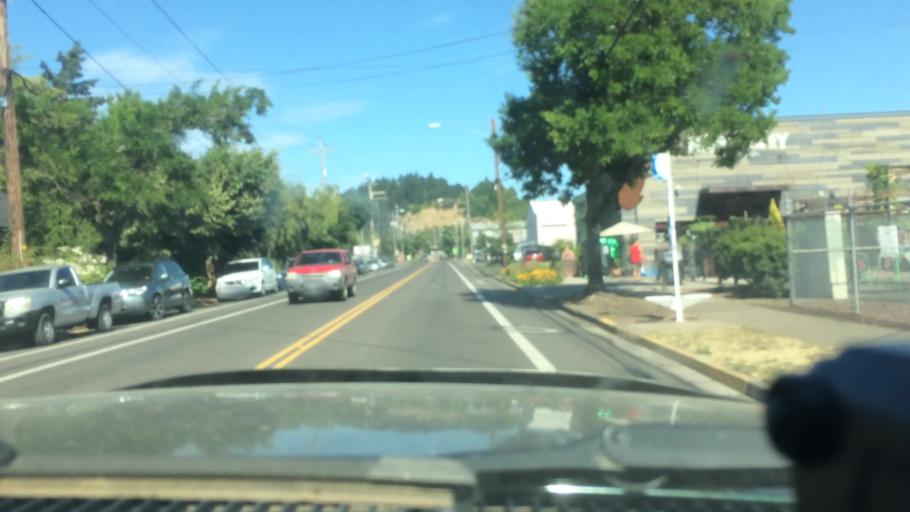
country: US
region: Oregon
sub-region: Lane County
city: Eugene
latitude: 44.0587
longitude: -123.1081
